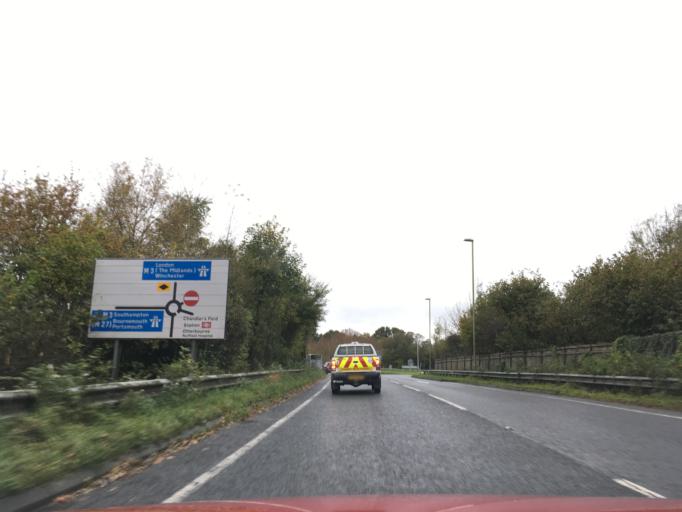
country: GB
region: England
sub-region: Hampshire
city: Eastleigh
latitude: 50.9942
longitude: -1.3559
